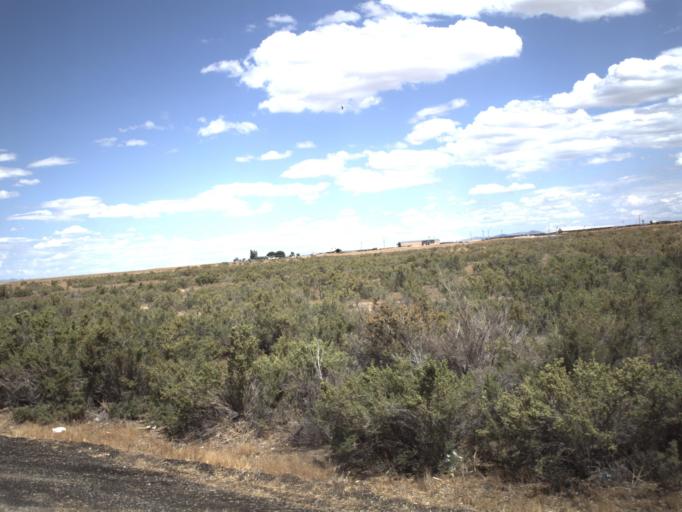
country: US
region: Utah
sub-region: Millard County
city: Delta
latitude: 39.3212
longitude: -112.4822
